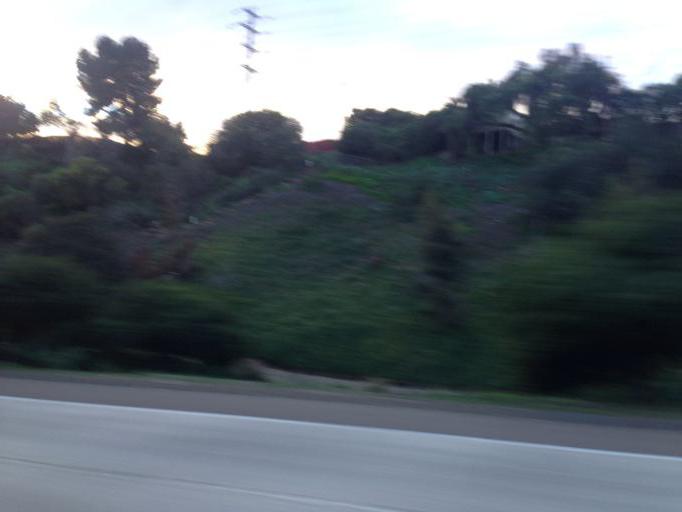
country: US
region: California
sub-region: San Diego County
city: San Diego
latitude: 32.7417
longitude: -117.1171
